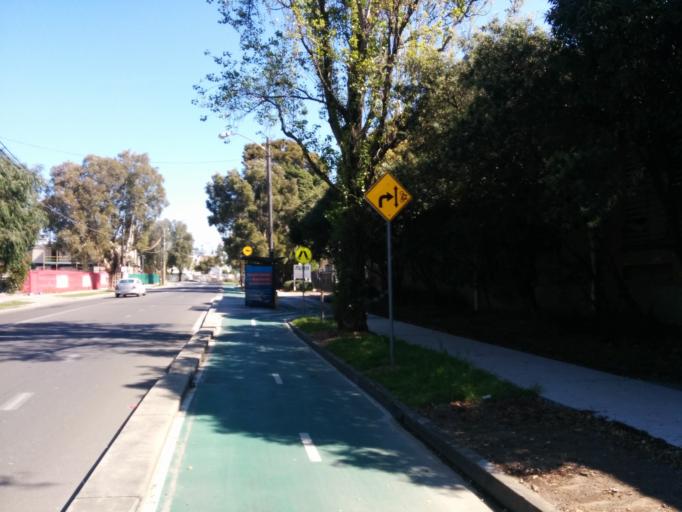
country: AU
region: New South Wales
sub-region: Botany Bay
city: Mascot
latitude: -33.9174
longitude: 151.1890
